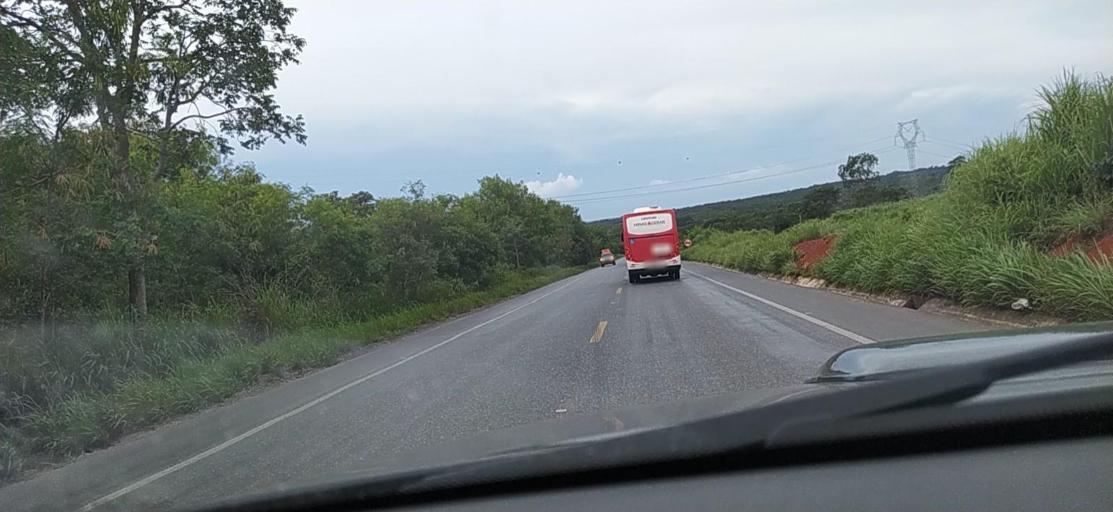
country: BR
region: Minas Gerais
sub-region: Montes Claros
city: Montes Claros
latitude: -16.6668
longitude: -43.7870
